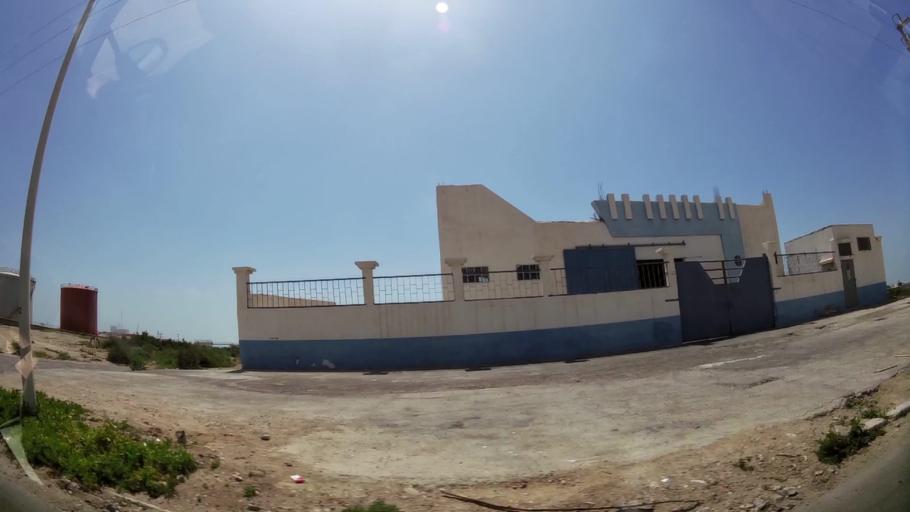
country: MA
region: Souss-Massa-Draa
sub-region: Agadir-Ida-ou-Tnan
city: Agadir
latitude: 30.4390
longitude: -9.6451
